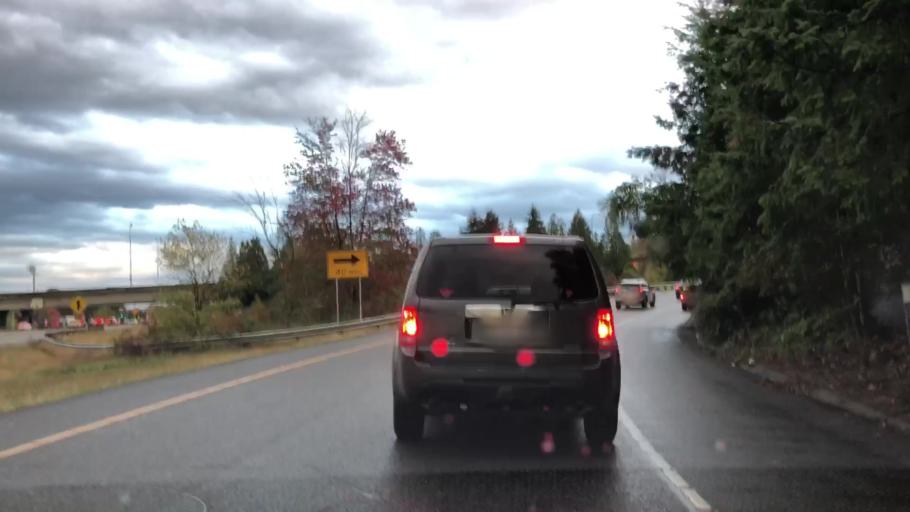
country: US
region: Washington
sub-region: King County
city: Eastgate
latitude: 47.5784
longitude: -122.1435
